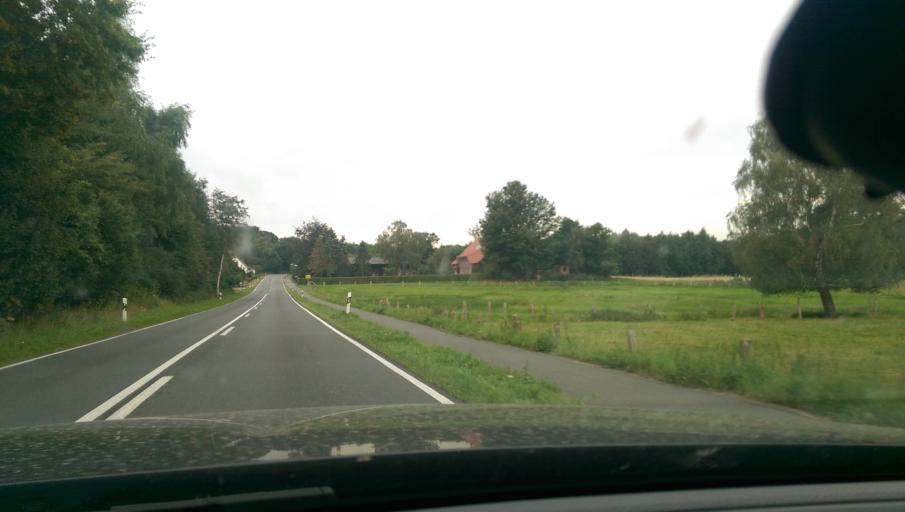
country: DE
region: Lower Saxony
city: Rehburg-Loccum
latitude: 52.4628
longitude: 9.1725
